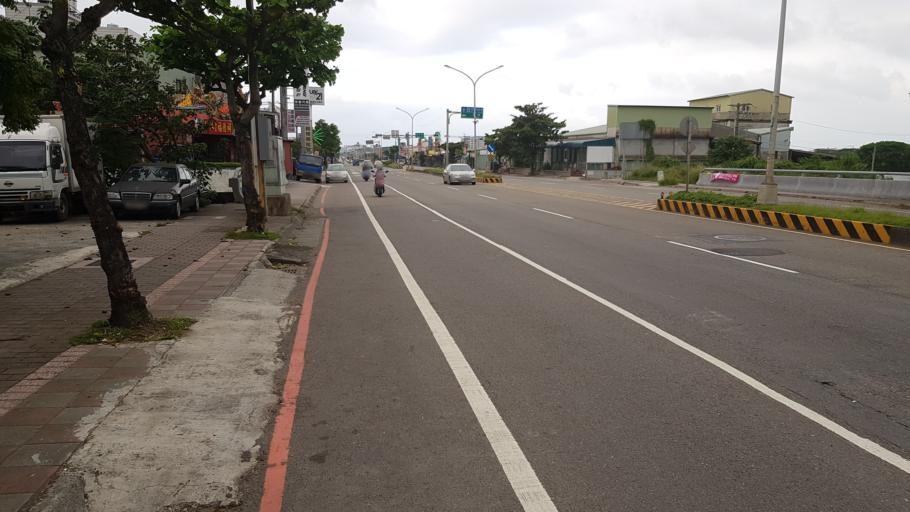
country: TW
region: Taiwan
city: Taoyuan City
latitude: 25.0806
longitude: 121.2580
